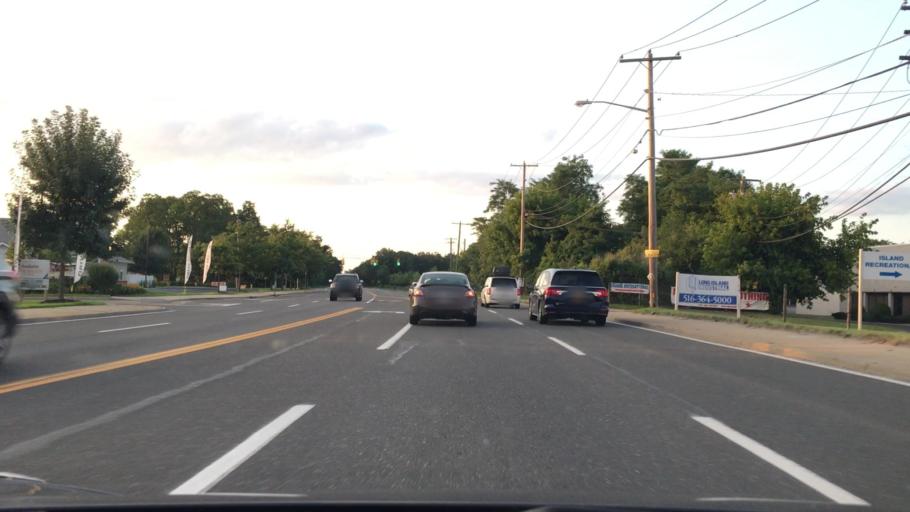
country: US
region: New York
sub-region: Suffolk County
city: Deer Park
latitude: 40.7673
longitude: -73.3106
